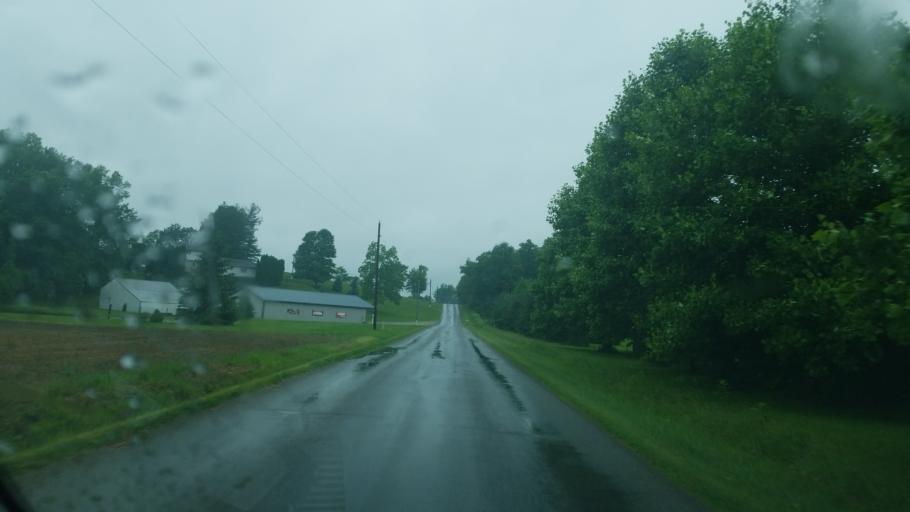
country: US
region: Ohio
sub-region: Huron County
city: Greenwich
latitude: 40.9385
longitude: -82.5592
